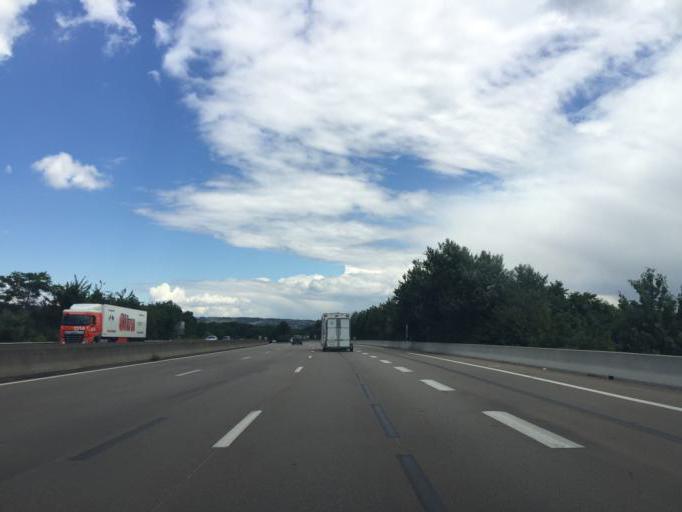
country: FR
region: Rhone-Alpes
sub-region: Departement de l'Isere
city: Auberives-sur-Vareze
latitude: 45.4130
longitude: 4.8254
